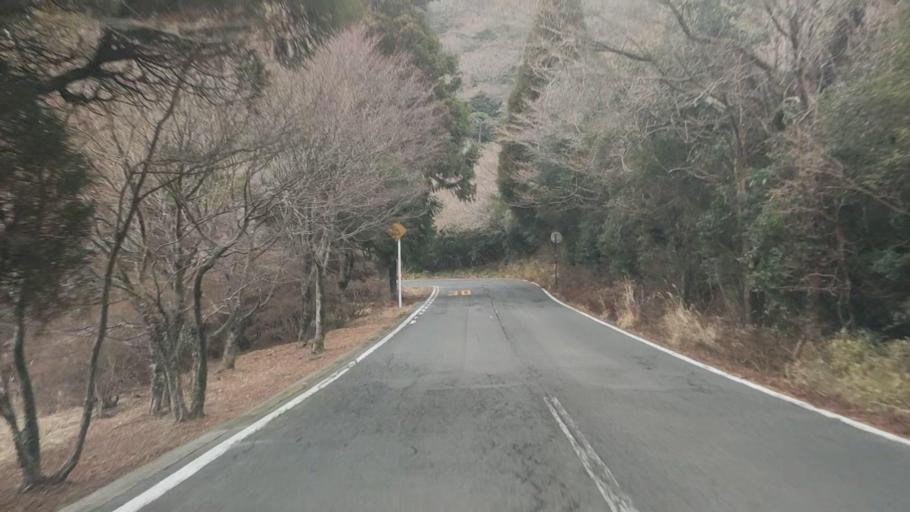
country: JP
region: Nagasaki
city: Shimabara
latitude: 32.7499
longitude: 130.2750
